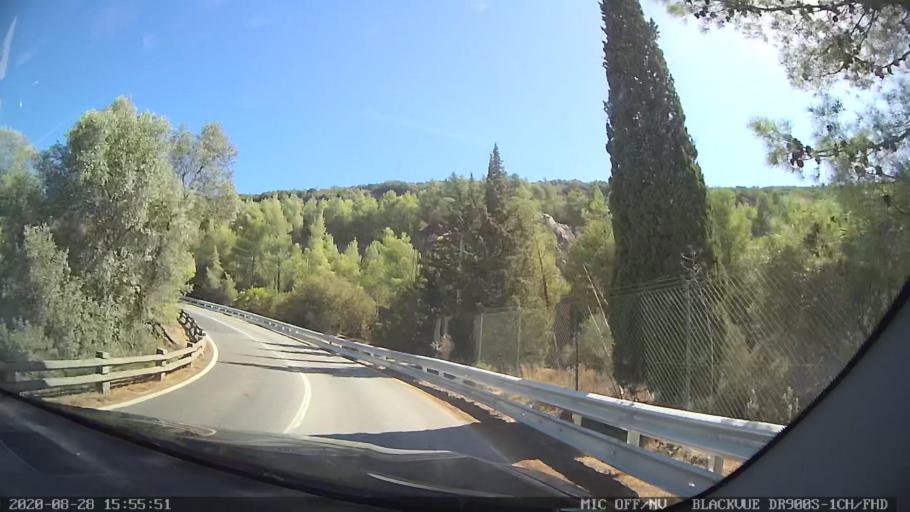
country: PT
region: Setubal
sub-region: Setubal
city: Setubal
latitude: 38.4938
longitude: -8.9419
